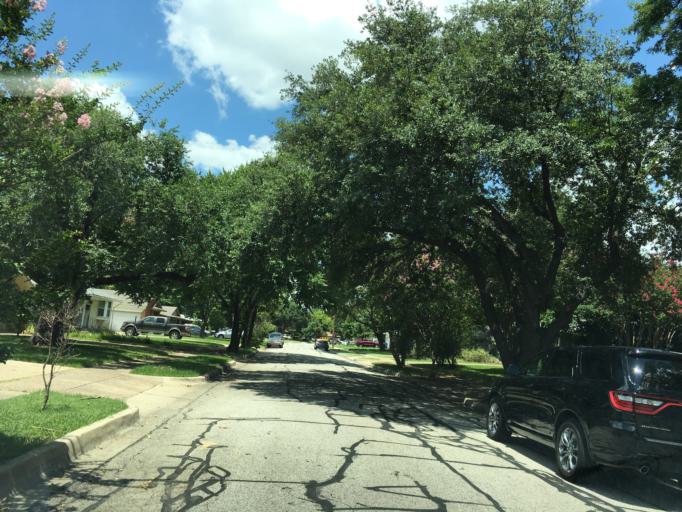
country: US
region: Texas
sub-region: Dallas County
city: Farmers Branch
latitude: 32.9250
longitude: -96.8694
